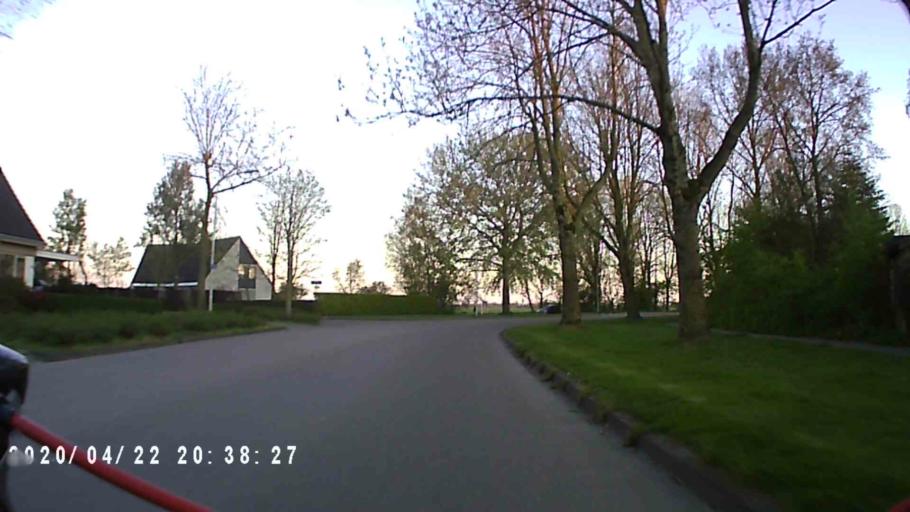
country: NL
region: Groningen
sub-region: Gemeente Winsum
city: Winsum
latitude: 53.3249
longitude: 6.5298
